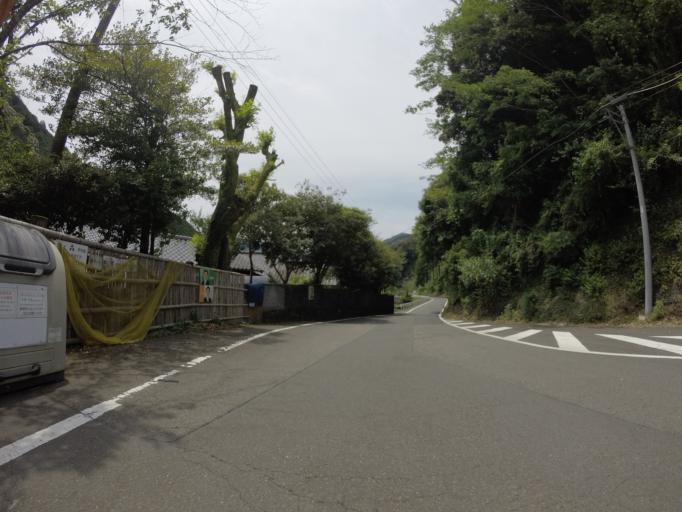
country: JP
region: Shizuoka
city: Shizuoka-shi
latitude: 35.0206
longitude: 138.2848
